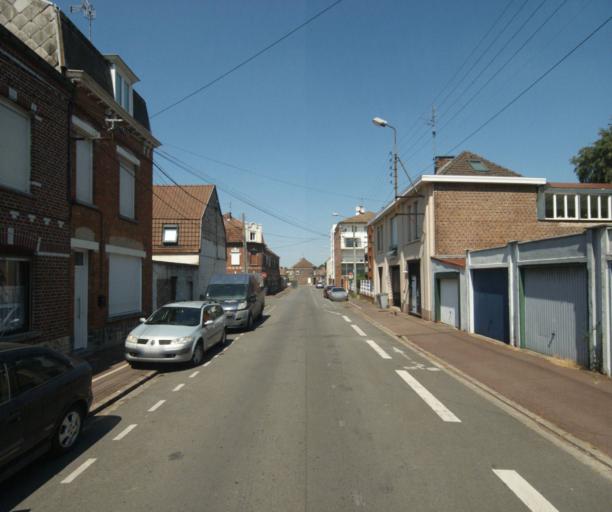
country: FR
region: Nord-Pas-de-Calais
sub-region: Departement du Nord
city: Halluin
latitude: 50.7821
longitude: 3.1219
